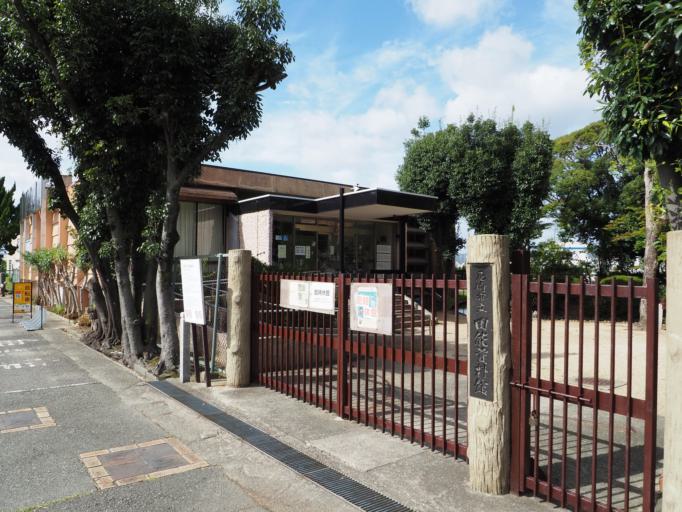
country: JP
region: Osaka
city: Toyonaka
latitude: 34.7698
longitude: 135.4400
